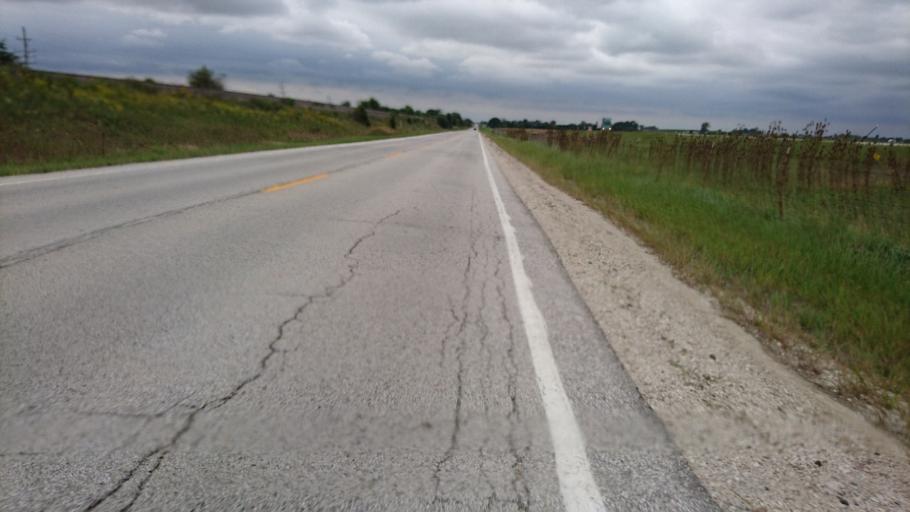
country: US
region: Illinois
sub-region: Livingston County
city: Odell
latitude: 40.9522
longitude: -88.5730
